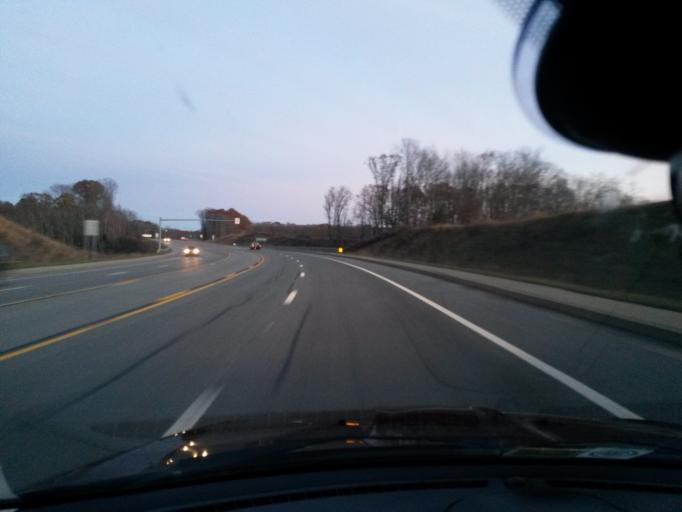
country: US
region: West Virginia
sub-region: Raleigh County
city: Stanaford
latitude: 37.7884
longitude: -81.1609
